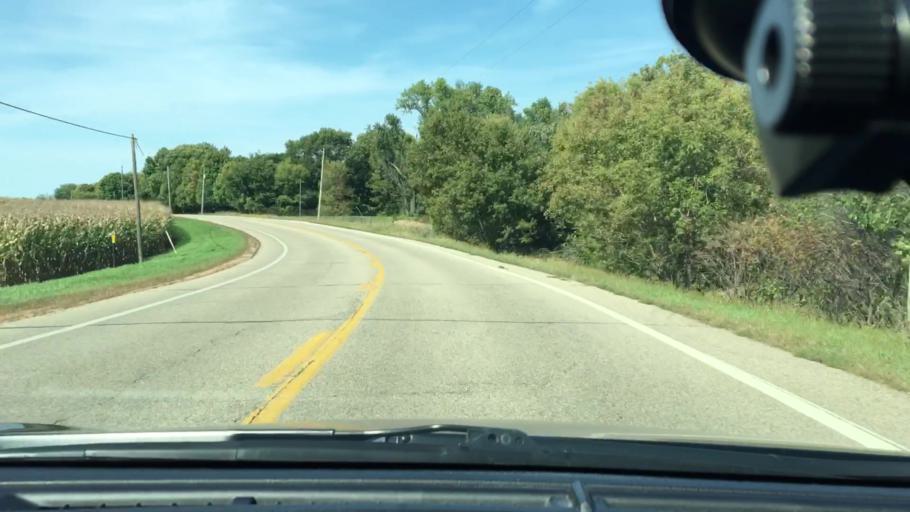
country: US
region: Minnesota
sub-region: Hennepin County
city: Corcoran
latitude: 45.1115
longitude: -93.5691
